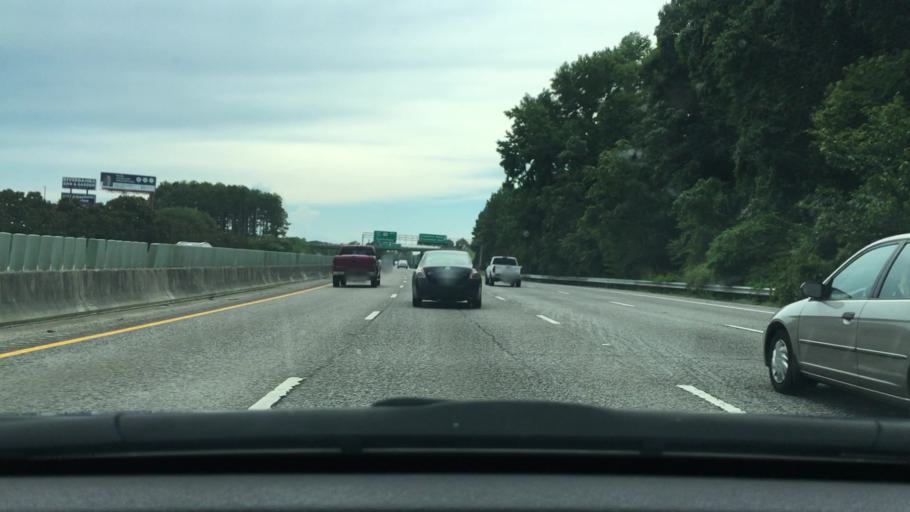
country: US
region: South Carolina
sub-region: Lexington County
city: West Columbia
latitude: 34.0121
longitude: -81.0708
